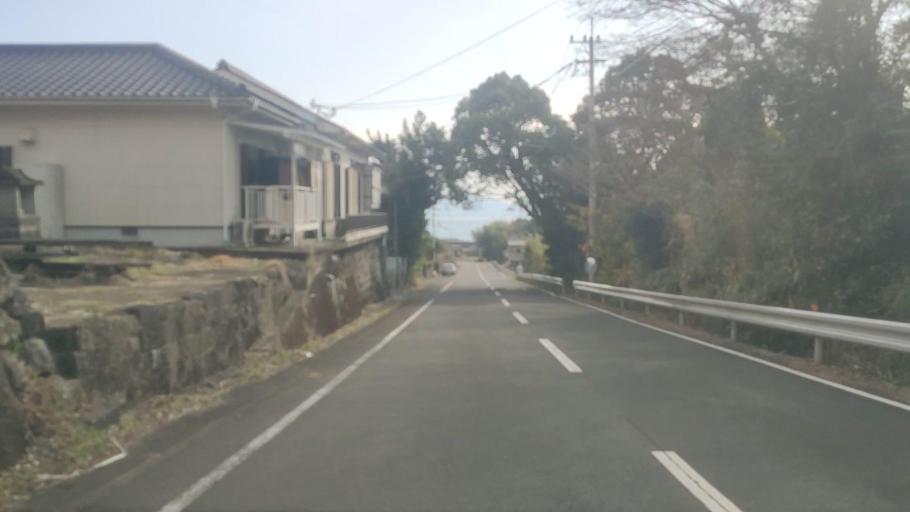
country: JP
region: Nagasaki
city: Shimabara
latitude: 32.6675
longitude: 130.2862
